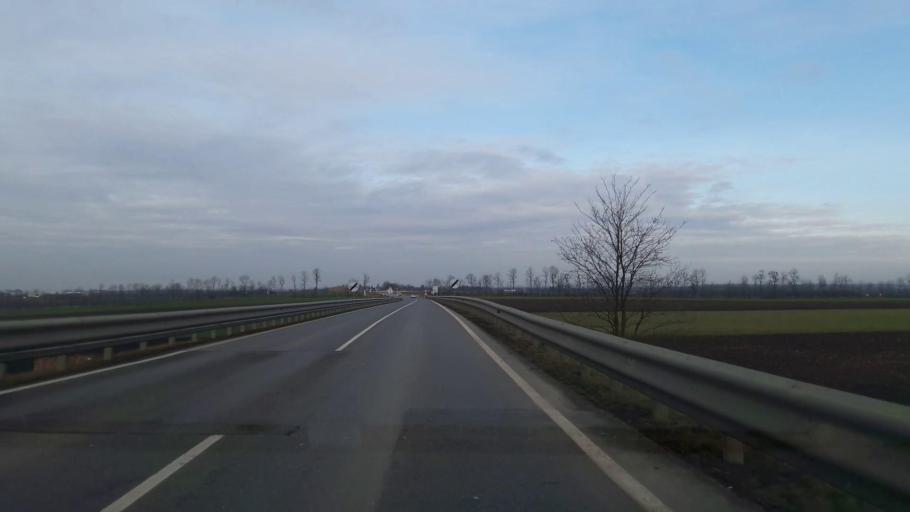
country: AT
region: Lower Austria
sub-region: Politischer Bezirk Mistelbach
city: Laa an der Thaya
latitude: 48.7126
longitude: 16.4234
